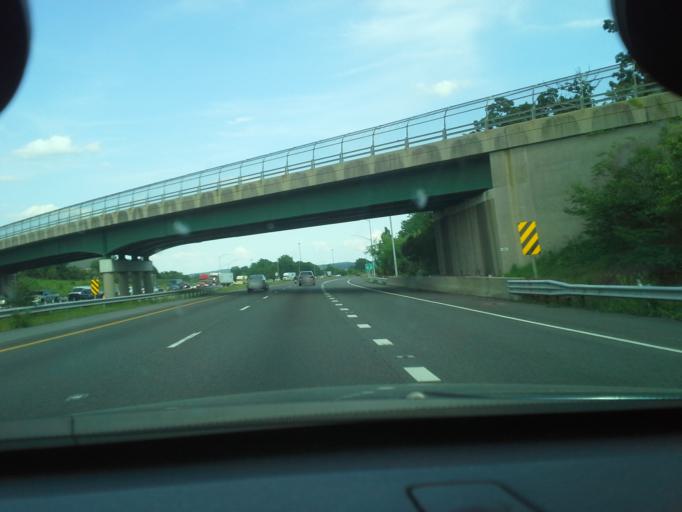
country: US
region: Maryland
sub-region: Frederick County
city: Ballenger Creek
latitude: 39.4019
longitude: -77.4476
